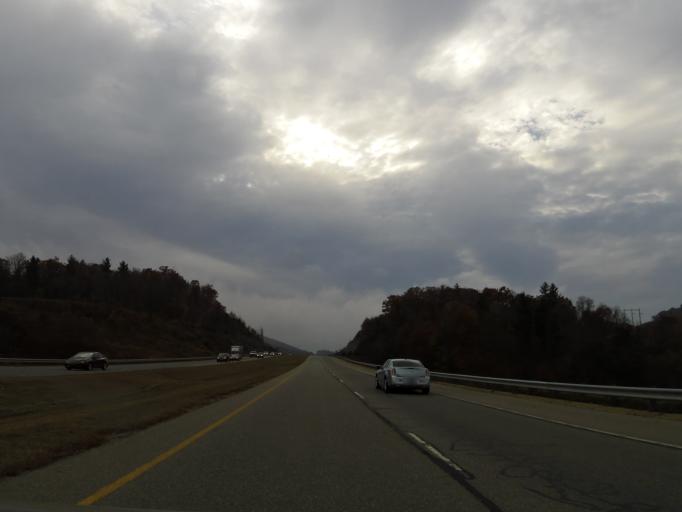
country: US
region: North Carolina
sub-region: Watauga County
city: Boone
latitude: 36.2297
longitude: -81.5973
